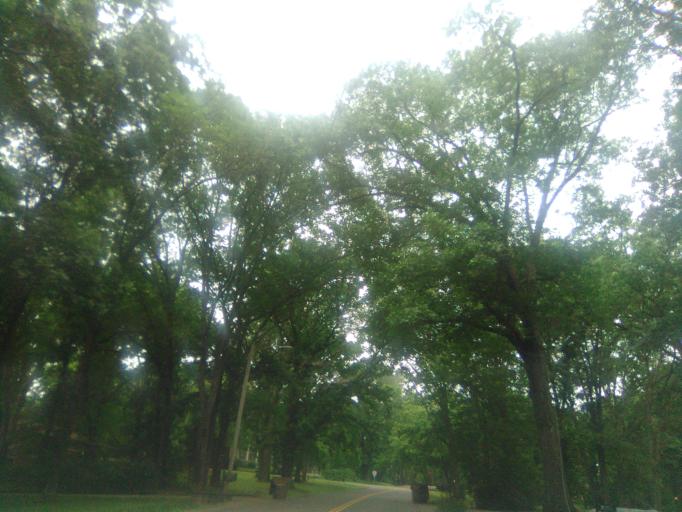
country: US
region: Tennessee
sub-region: Davidson County
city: Belle Meade
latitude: 36.1095
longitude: -86.8806
